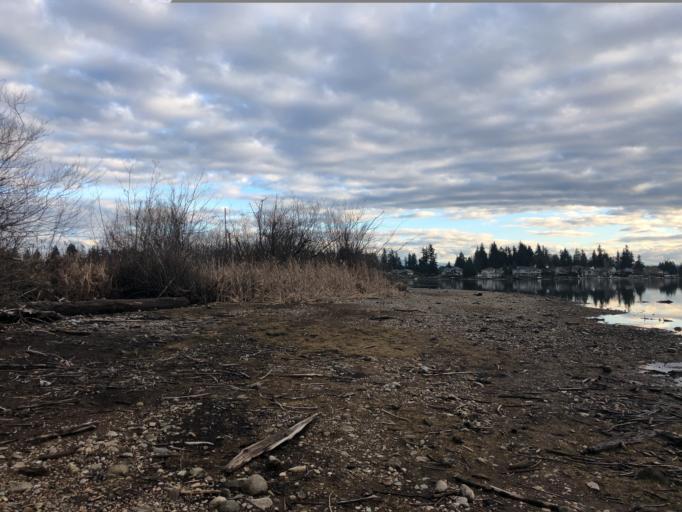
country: US
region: Washington
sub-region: Pierce County
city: Bonney Lake
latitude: 47.2375
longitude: -122.1615
